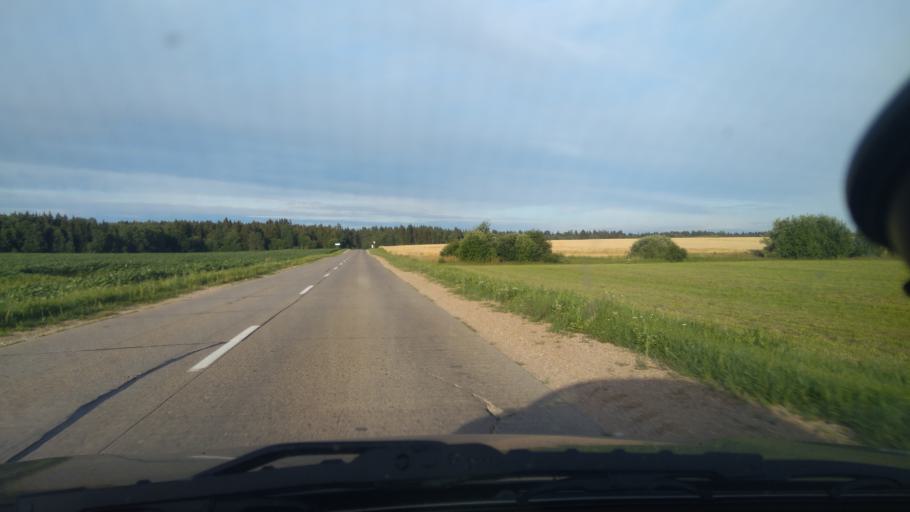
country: BY
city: Michanovichi
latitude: 53.6086
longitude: 27.6646
